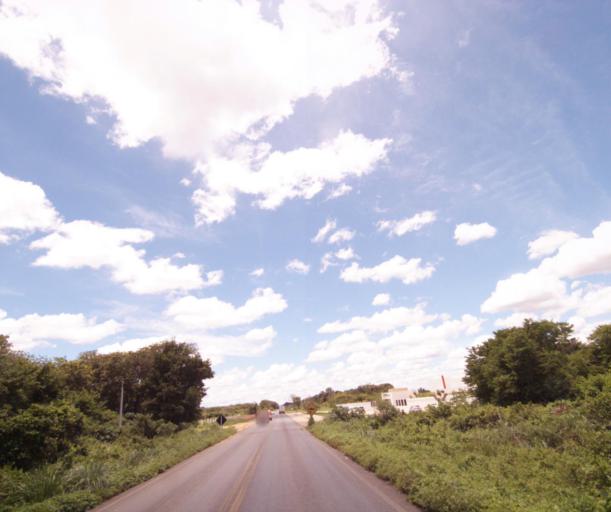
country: BR
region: Bahia
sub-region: Bom Jesus Da Lapa
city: Bom Jesus da Lapa
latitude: -13.2629
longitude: -43.5458
